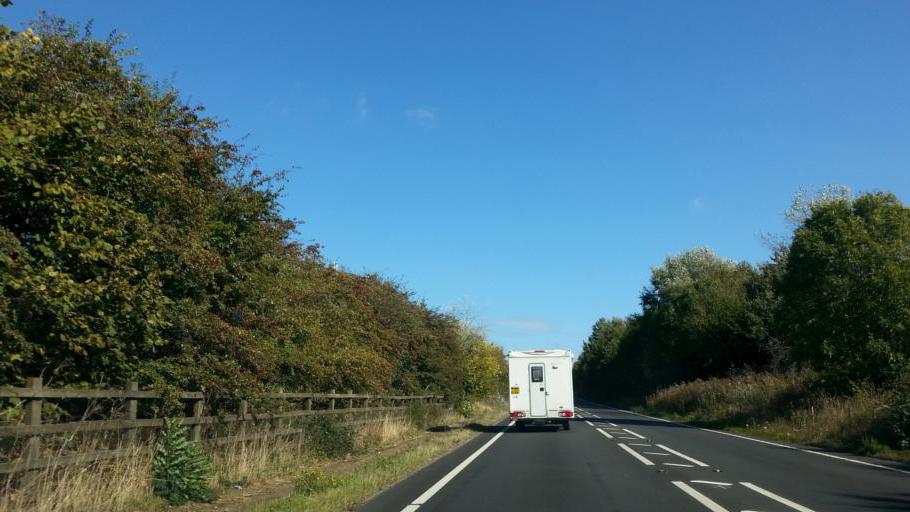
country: GB
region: England
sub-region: Northamptonshire
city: Oundle
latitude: 52.5139
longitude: -0.4138
